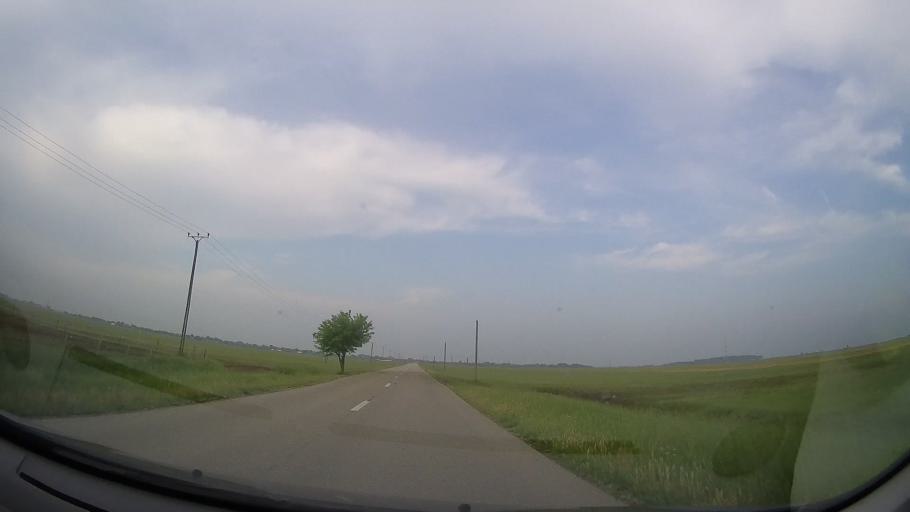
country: RO
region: Timis
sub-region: Comuna Foeni
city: Foeni
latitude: 45.5095
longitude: 20.8895
